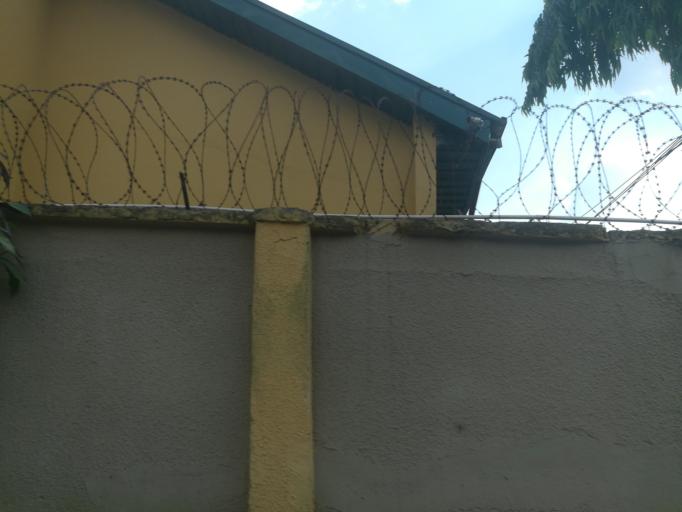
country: NG
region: Abuja Federal Capital Territory
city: Abuja
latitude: 9.0833
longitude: 7.4151
